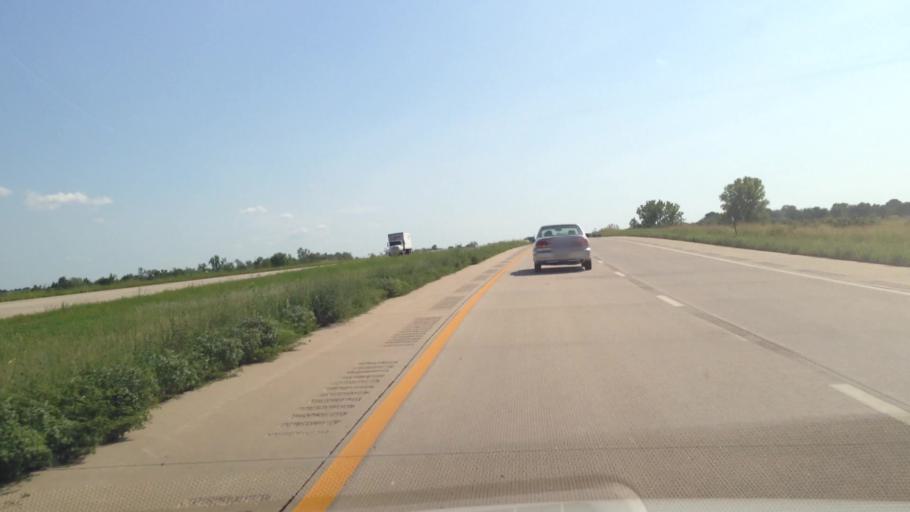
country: US
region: Kansas
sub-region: Bourbon County
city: Fort Scott
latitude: 37.9700
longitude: -94.7051
